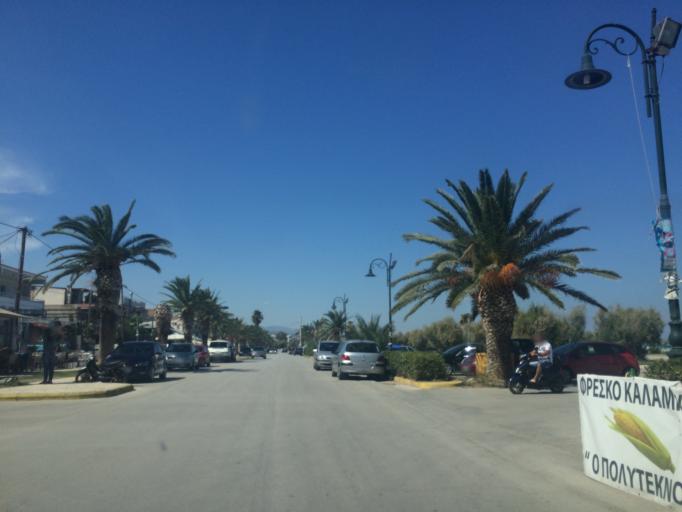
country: GR
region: Peloponnese
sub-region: Nomos Korinthias
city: Vrakhati
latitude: 37.9621
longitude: 22.8070
